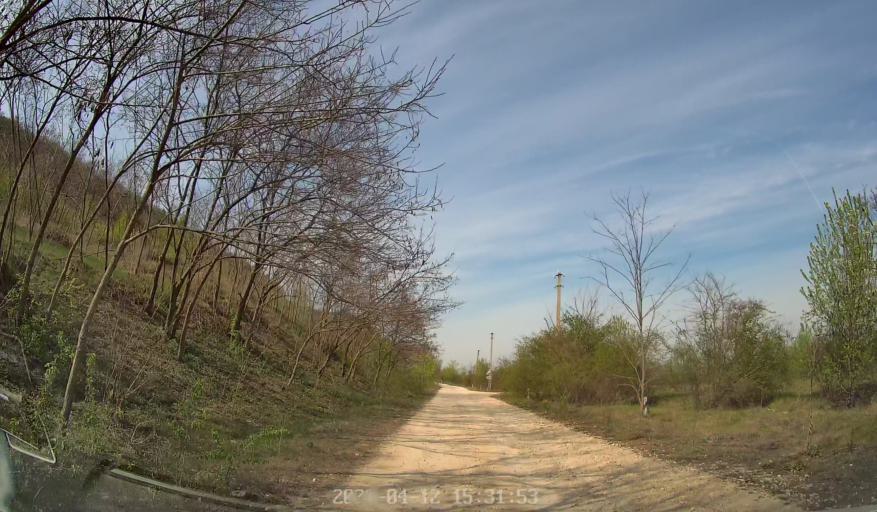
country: MD
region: Telenesti
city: Cocieri
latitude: 47.3247
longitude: 29.0739
